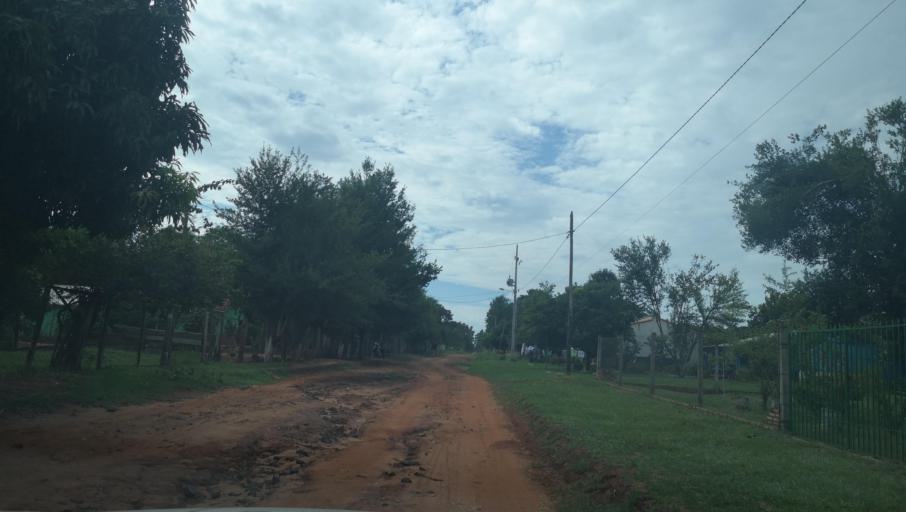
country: PY
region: San Pedro
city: Capiibary
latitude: -24.7195
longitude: -56.0224
